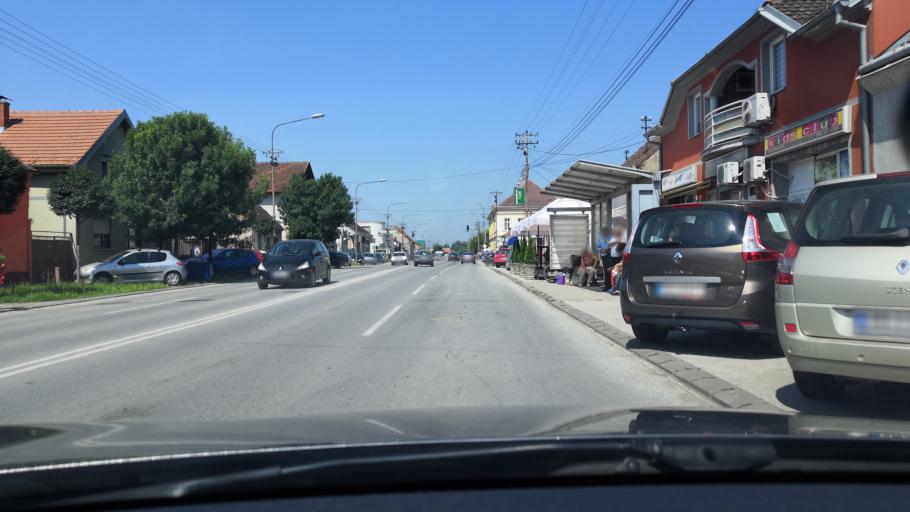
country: RS
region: Autonomna Pokrajina Vojvodina
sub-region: Sremski Okrug
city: Sremska Mitrovica
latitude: 44.9724
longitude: 19.6083
